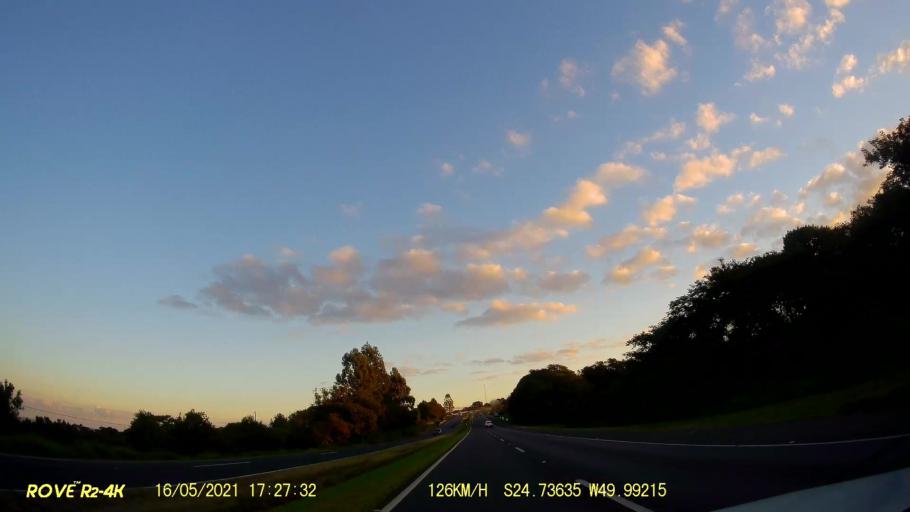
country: BR
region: Parana
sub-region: Castro
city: Castro
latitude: -24.7366
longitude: -49.9923
